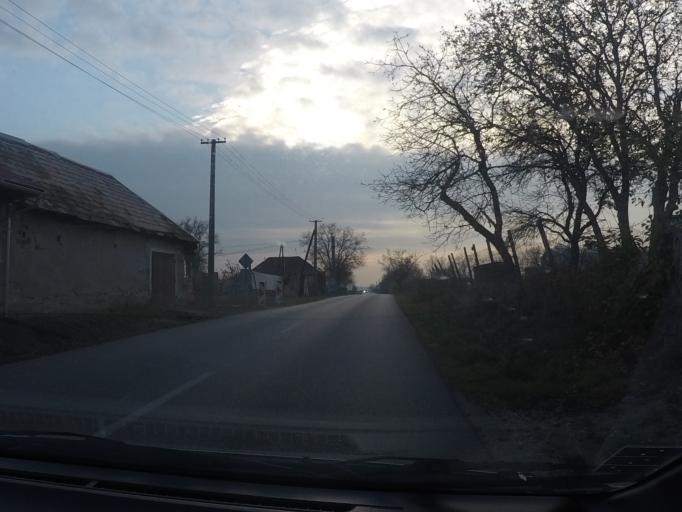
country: SK
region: Nitriansky
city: Zeliezovce
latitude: 48.1003
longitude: 18.5307
